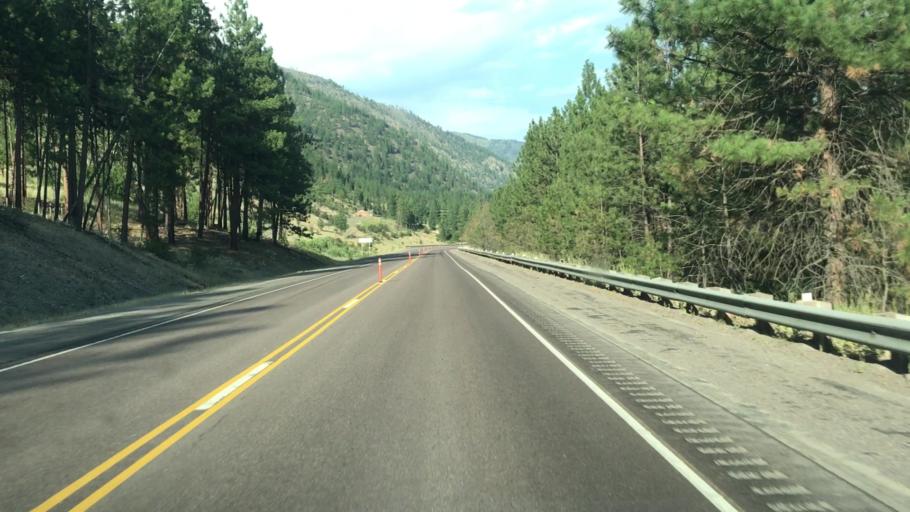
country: US
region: Montana
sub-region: Mineral County
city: Superior
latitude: 47.0177
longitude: -114.6829
